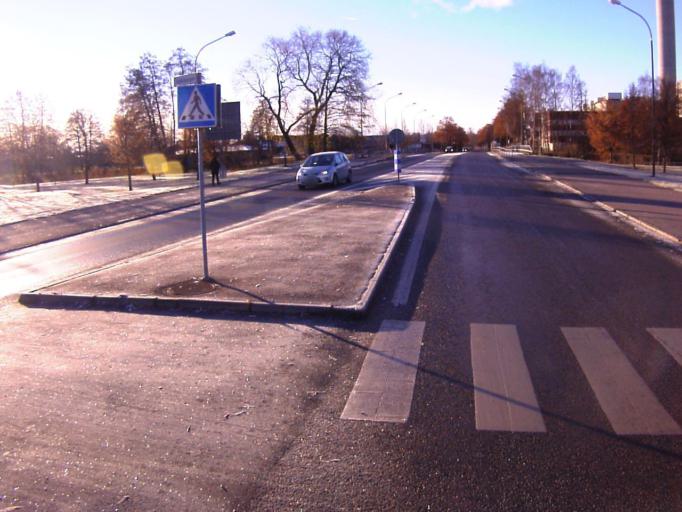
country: SE
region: Soedermanland
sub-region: Eskilstuna Kommun
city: Eskilstuna
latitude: 59.3820
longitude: 16.4997
